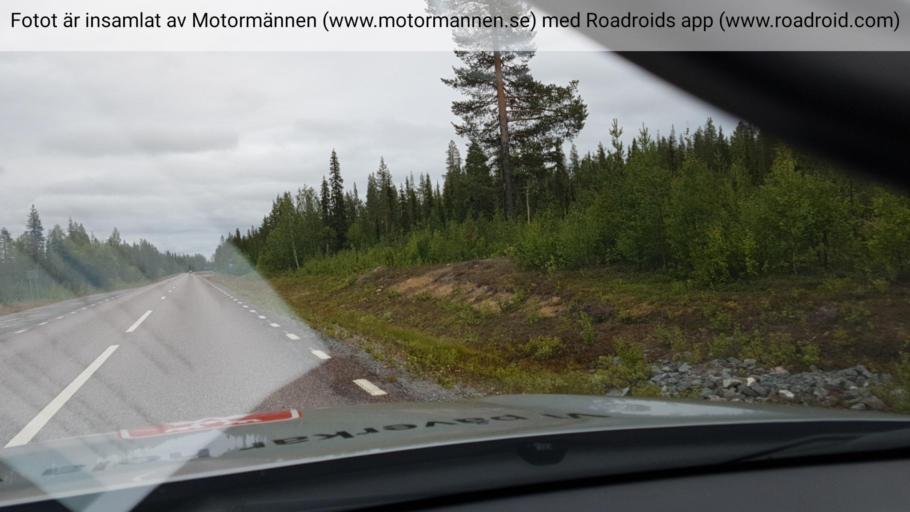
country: SE
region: Norrbotten
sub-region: Gallivare Kommun
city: Gaellivare
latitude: 67.0708
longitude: 21.5335
